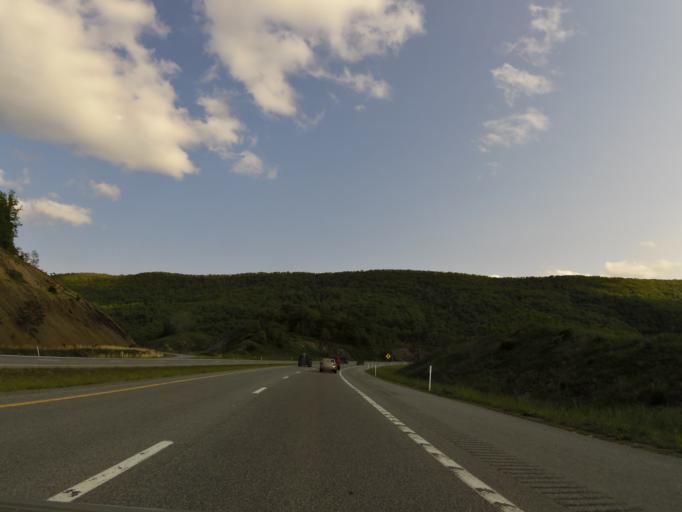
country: US
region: West Virginia
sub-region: Mercer County
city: Bluefield
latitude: 37.2778
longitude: -81.1646
